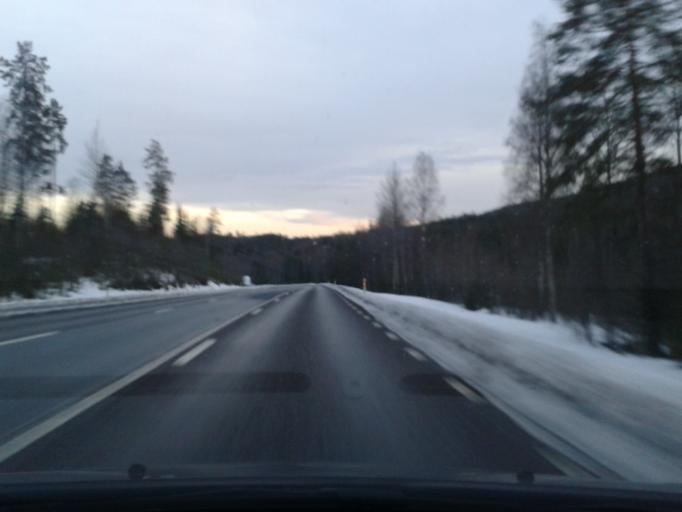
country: SE
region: Vaesternorrland
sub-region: Kramfors Kommun
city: Bollstabruk
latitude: 63.1050
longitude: 17.5090
